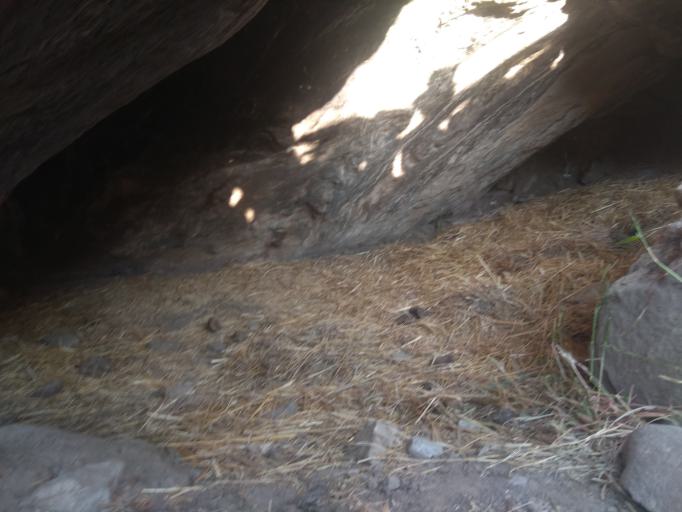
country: NP
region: Mid Western
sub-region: Bheri Zone
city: Dailekh
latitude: 29.2789
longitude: 81.7327
